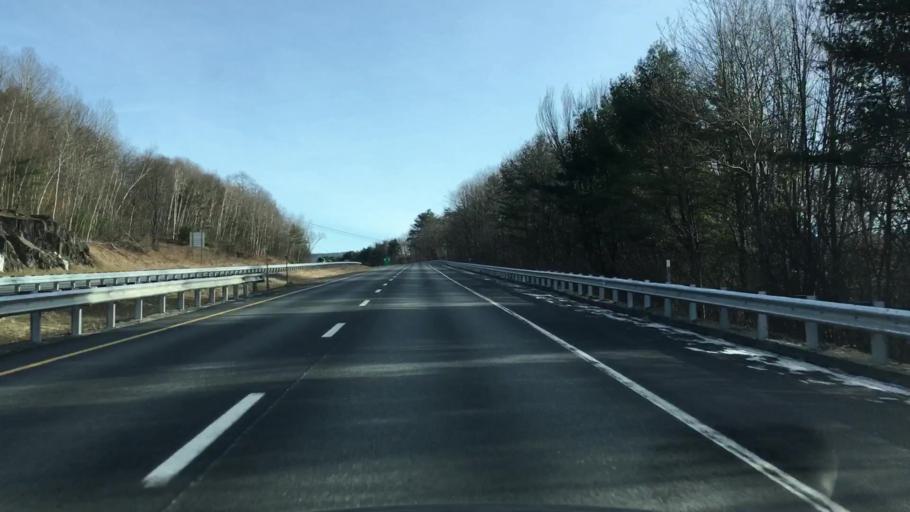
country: US
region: New Hampshire
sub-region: Grafton County
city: Lebanon
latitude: 43.6436
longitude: -72.2311
